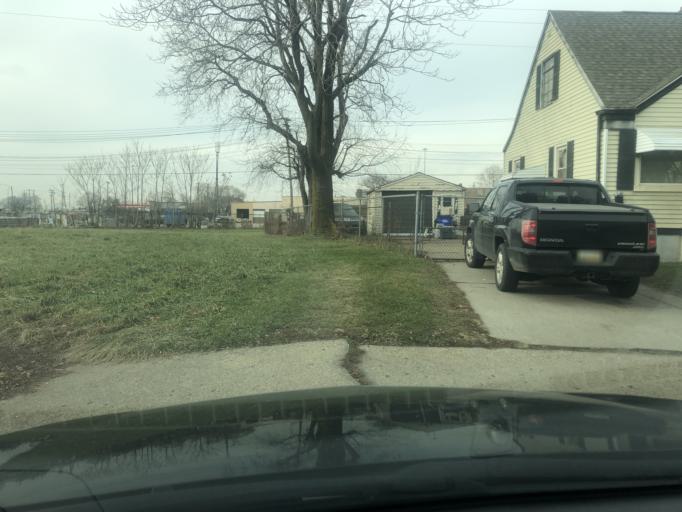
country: US
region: Michigan
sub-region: Wayne County
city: River Rouge
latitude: 42.2759
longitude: -83.1522
